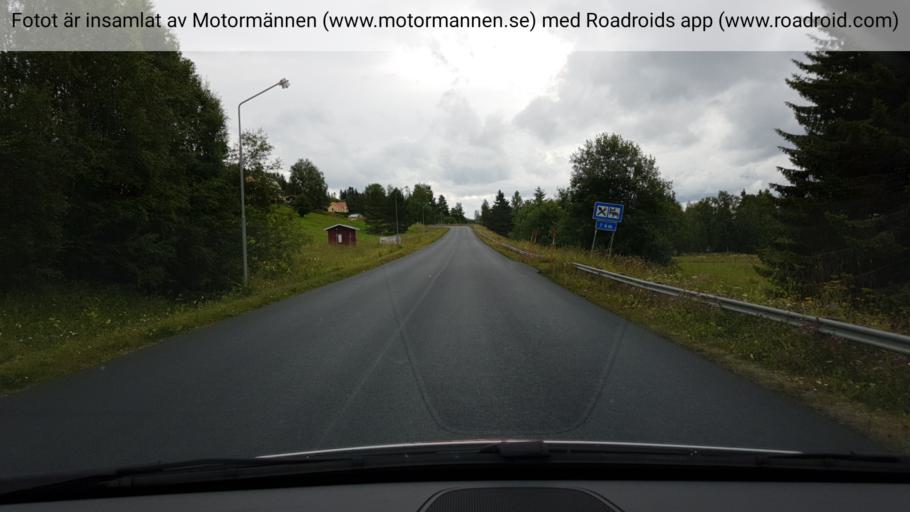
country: SE
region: Jaemtland
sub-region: Krokoms Kommun
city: Krokom
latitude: 63.6729
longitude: 14.5943
